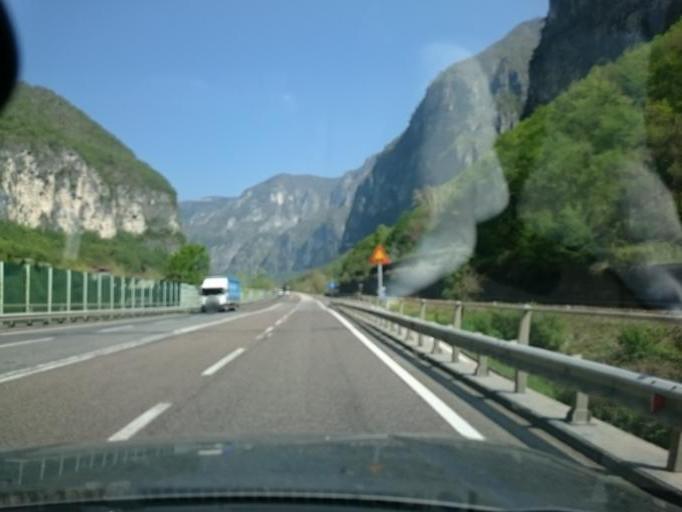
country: IT
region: Veneto
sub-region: Provincia di Vicenza
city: Cismon del Grappa
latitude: 45.8995
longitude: 11.6951
